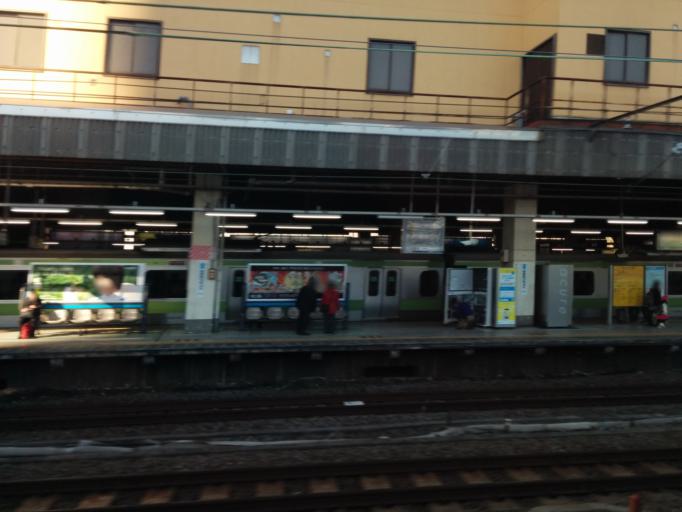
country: JP
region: Tokyo
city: Tokyo
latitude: 35.6548
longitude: 139.7571
